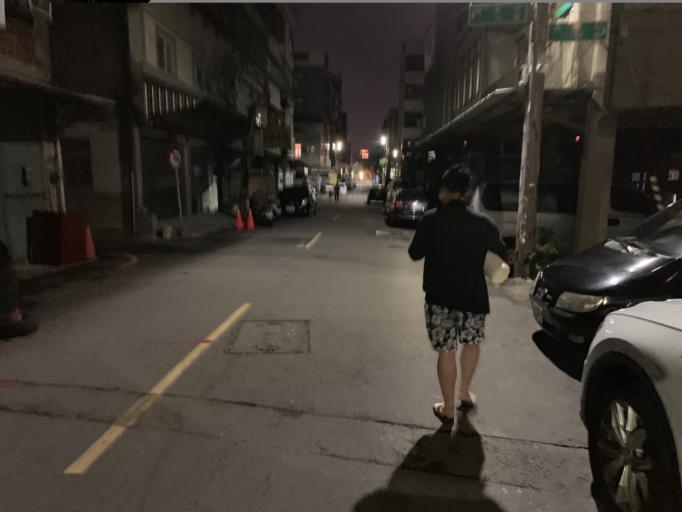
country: TW
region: Taiwan
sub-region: Hsinchu
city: Hsinchu
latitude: 24.7974
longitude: 120.9670
